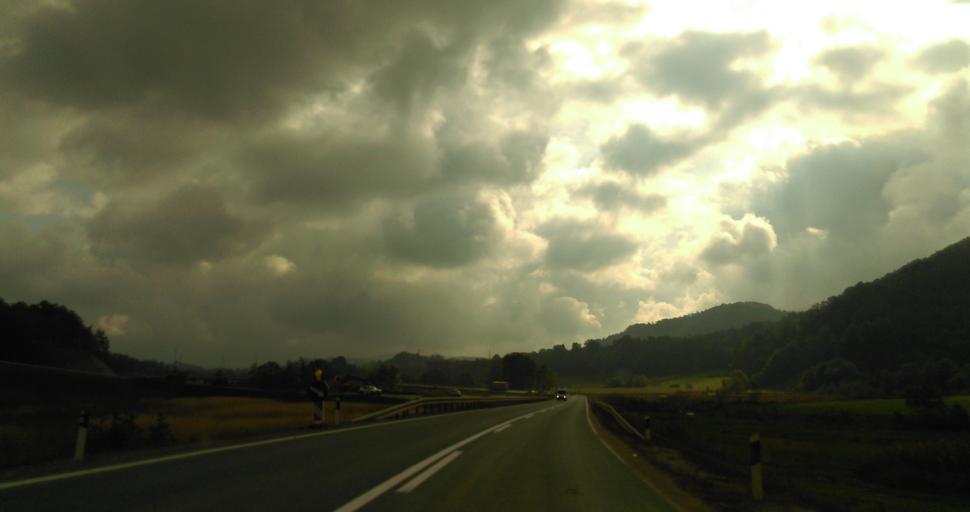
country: RS
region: Central Serbia
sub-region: Kolubarski Okrug
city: Ljig
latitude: 44.1995
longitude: 20.2688
